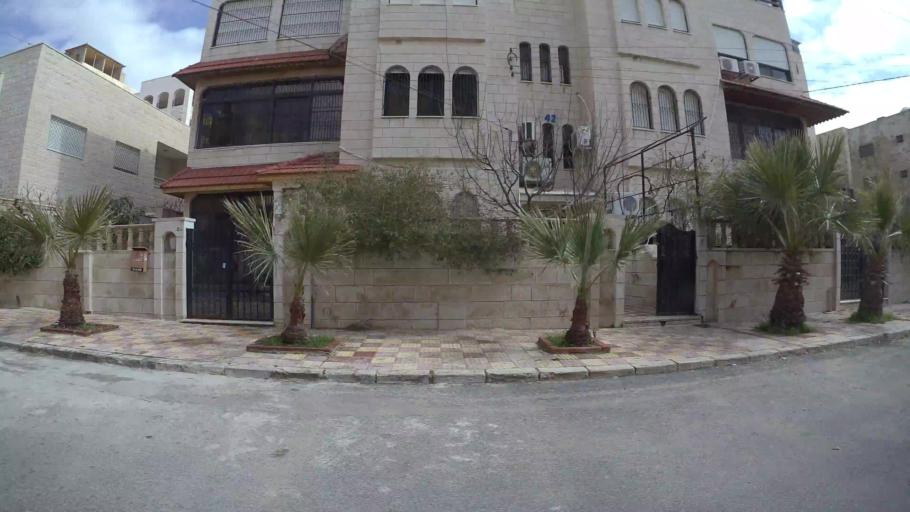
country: JO
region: Amman
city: Al Jubayhah
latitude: 31.9923
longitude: 35.8509
